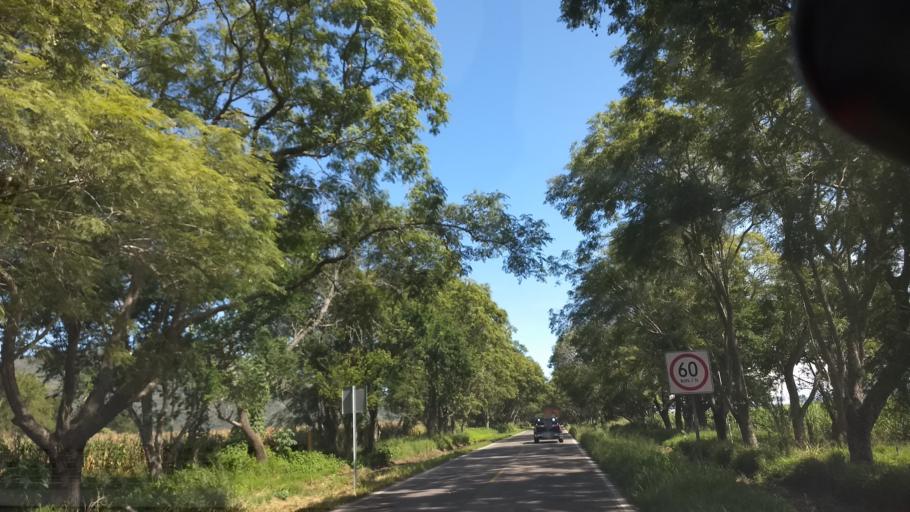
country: MX
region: Jalisco
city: Tuxpan
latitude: 19.5312
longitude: -103.4196
